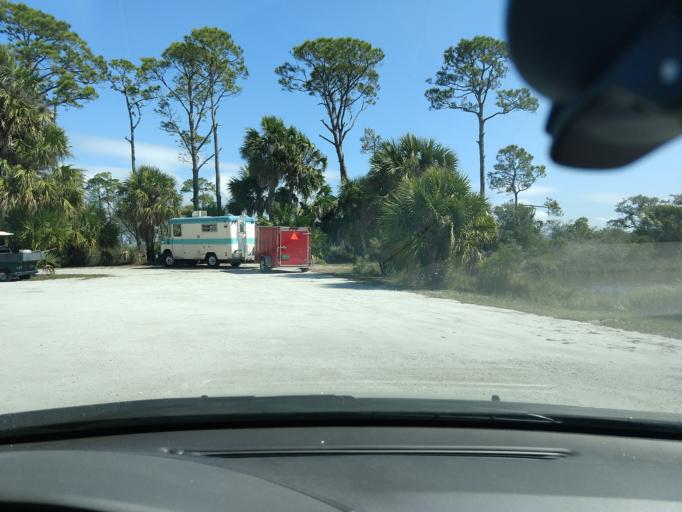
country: US
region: Florida
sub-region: Gulf County
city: Port Saint Joe
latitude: 29.7763
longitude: -85.4023
